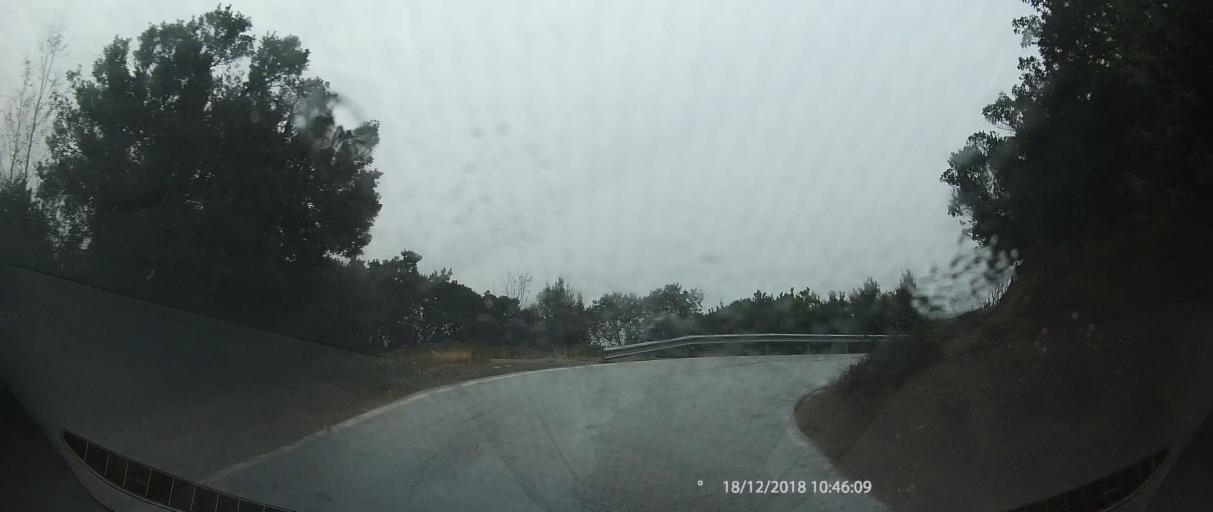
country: GR
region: Central Macedonia
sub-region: Nomos Pierias
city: Kato Milia
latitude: 40.1889
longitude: 22.3247
